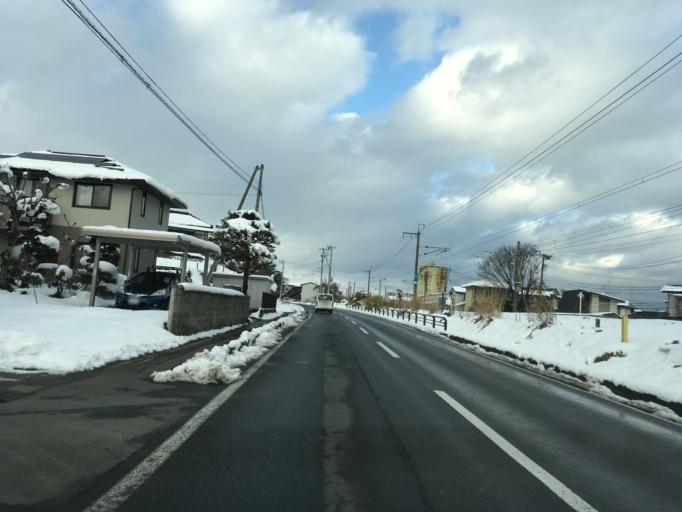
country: JP
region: Iwate
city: Mizusawa
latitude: 39.1322
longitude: 141.1464
